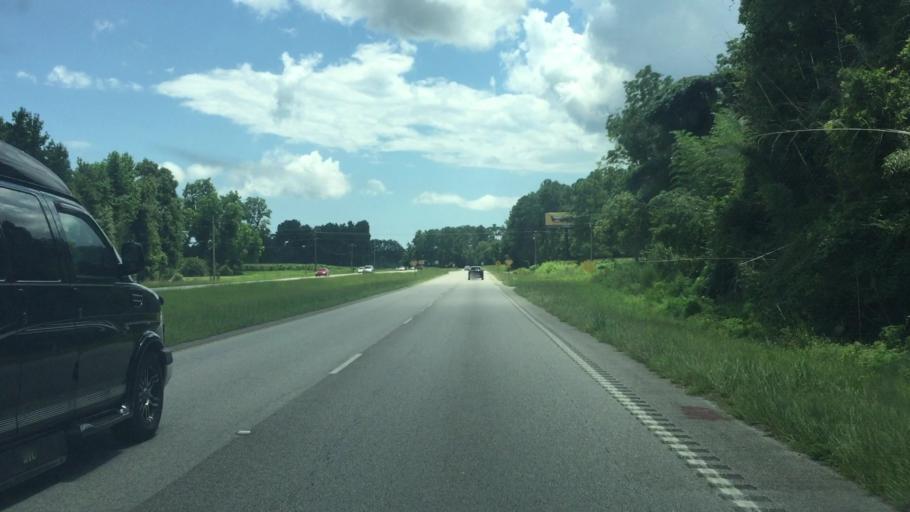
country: US
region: South Carolina
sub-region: Horry County
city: Little River
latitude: 33.9464
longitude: -78.7355
